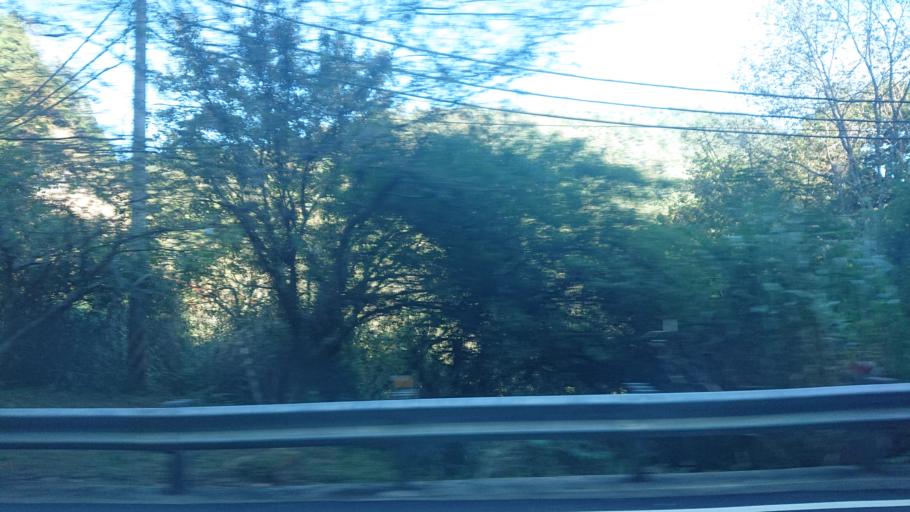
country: TW
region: Taiwan
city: Lugu
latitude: 23.5058
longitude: 120.8162
